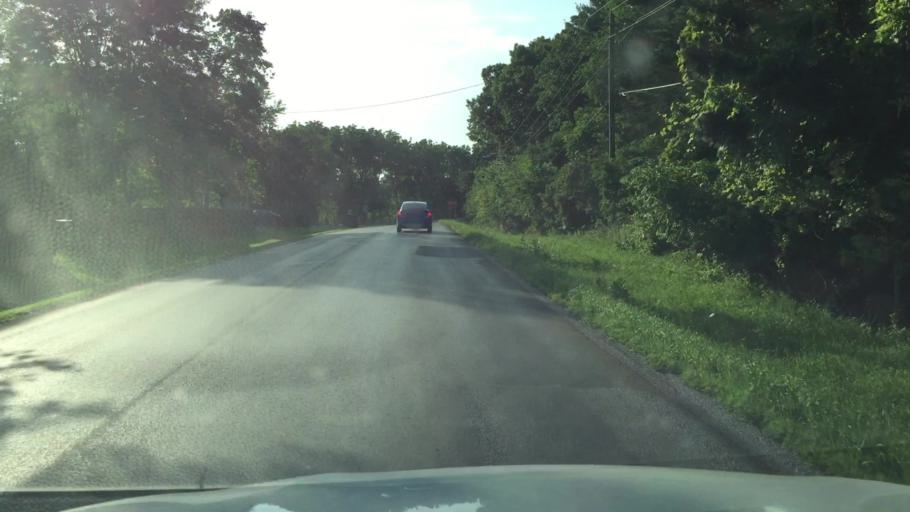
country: US
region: Iowa
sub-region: Linn County
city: Ely
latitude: 41.8339
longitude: -91.6344
